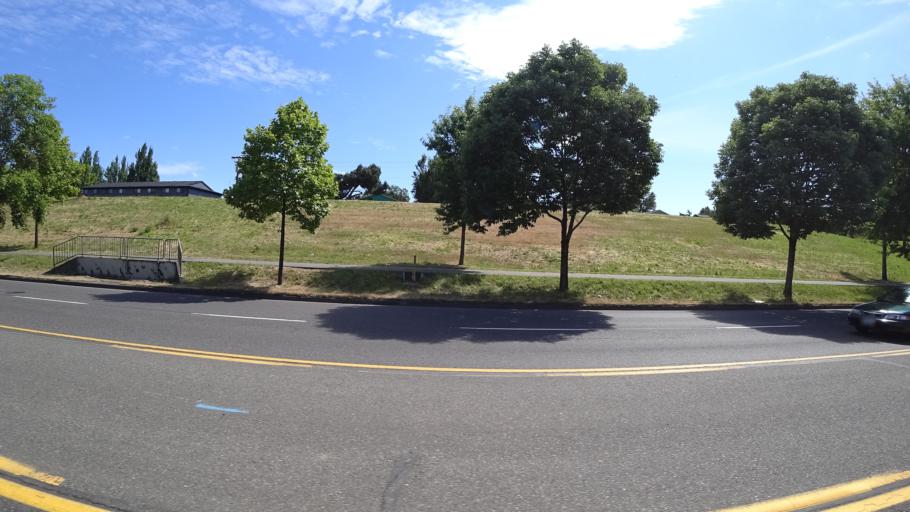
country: US
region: Washington
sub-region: Clark County
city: Vancouver
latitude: 45.5917
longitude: -122.7079
